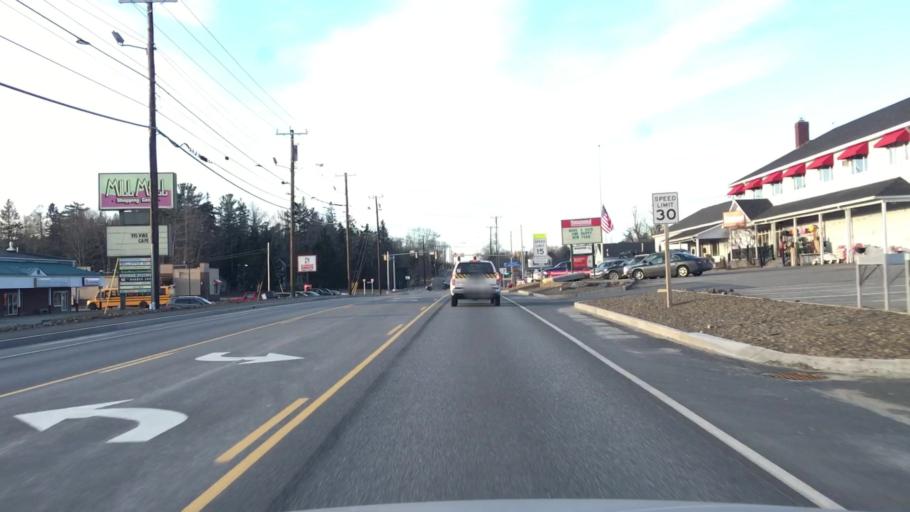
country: US
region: Maine
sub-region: Hancock County
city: Ellsworth
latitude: 44.5518
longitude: -68.4284
